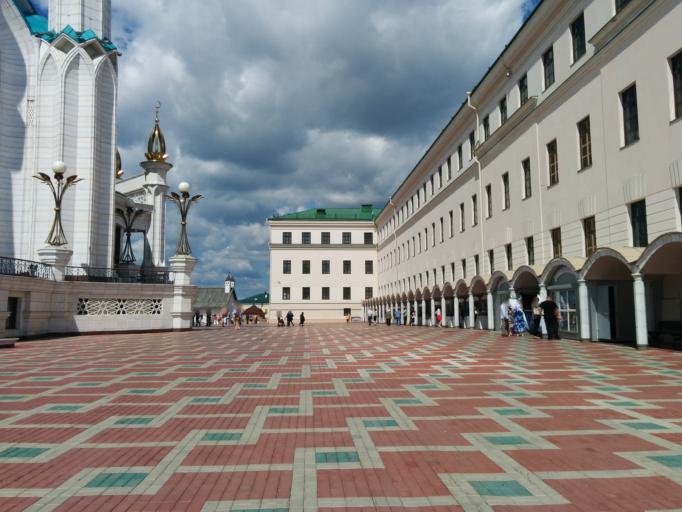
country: RU
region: Tatarstan
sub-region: Gorod Kazan'
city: Kazan
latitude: 55.7982
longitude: 49.1059
